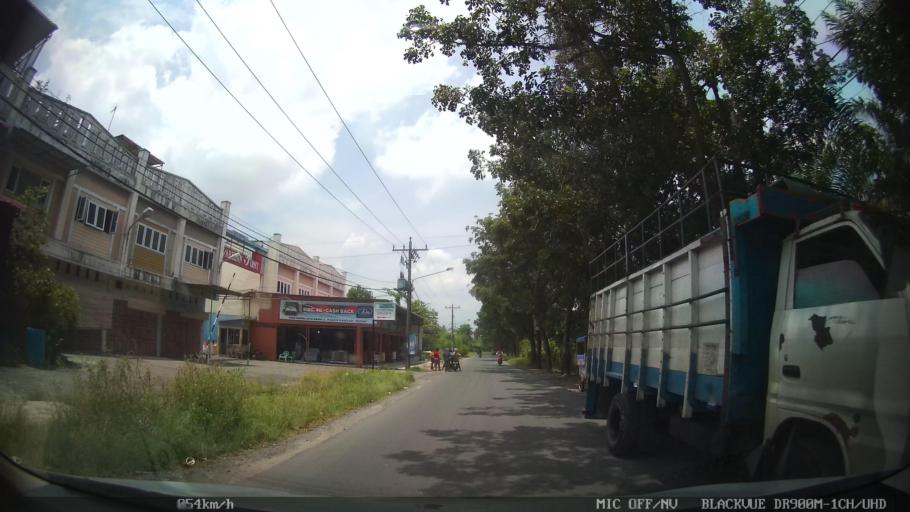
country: ID
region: North Sumatra
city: Labuhan Deli
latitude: 3.7095
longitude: 98.6672
